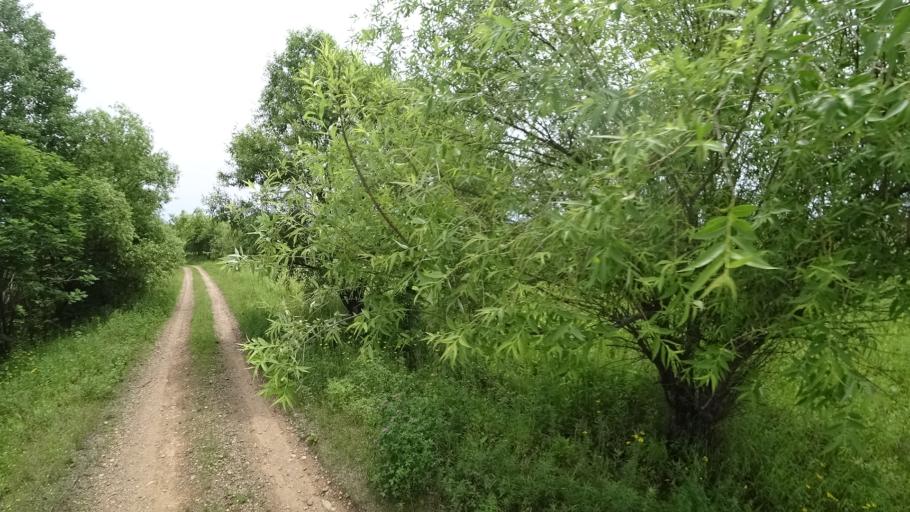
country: RU
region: Primorskiy
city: Arsen'yev
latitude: 44.1825
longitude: 133.3194
